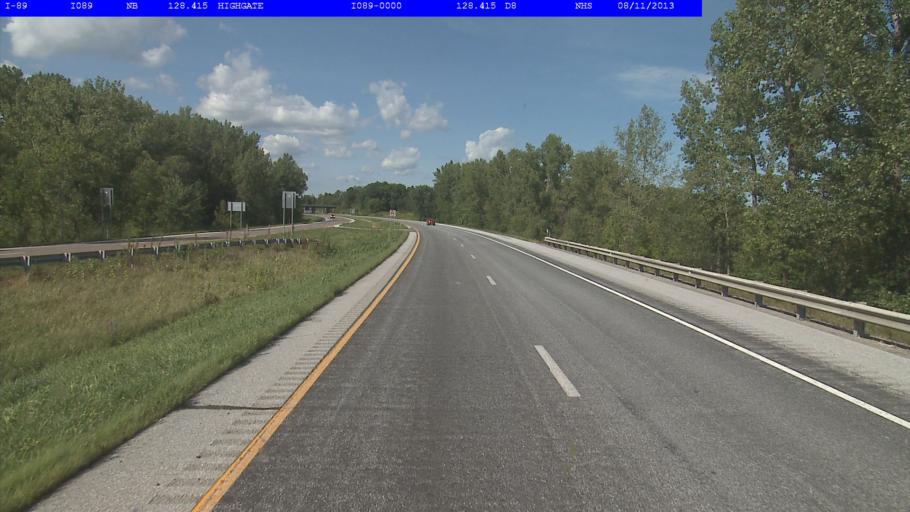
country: US
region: Vermont
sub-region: Franklin County
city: Swanton
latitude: 44.9891
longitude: -73.0861
